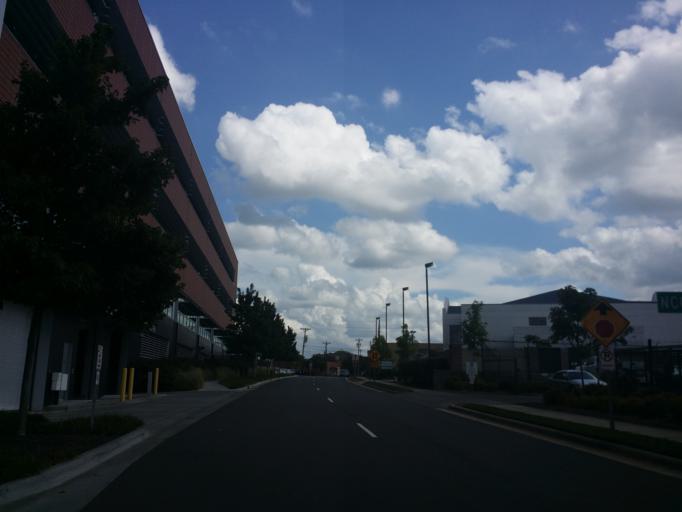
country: US
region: North Carolina
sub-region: Durham County
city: Durham
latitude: 35.9919
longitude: -78.8975
